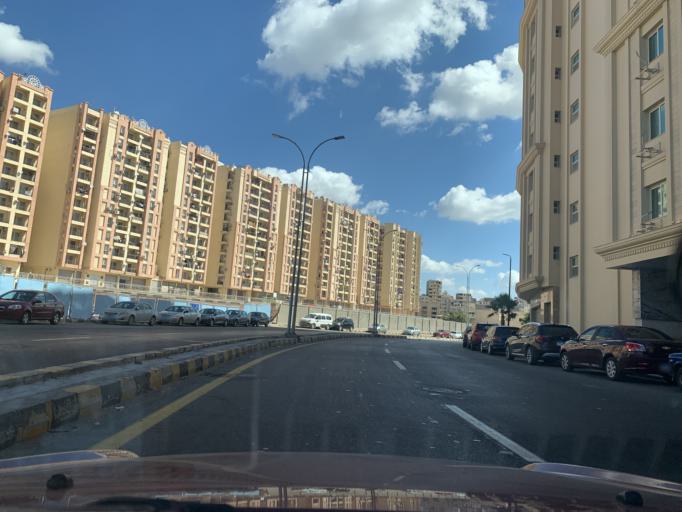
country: EG
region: Alexandria
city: Alexandria
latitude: 31.2168
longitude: 29.9584
